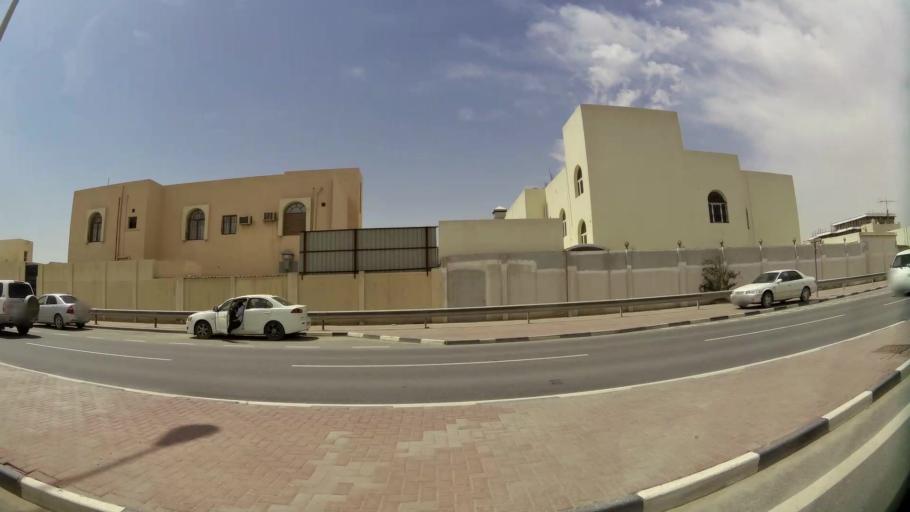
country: QA
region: Baladiyat ar Rayyan
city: Ar Rayyan
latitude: 25.2936
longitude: 51.4128
